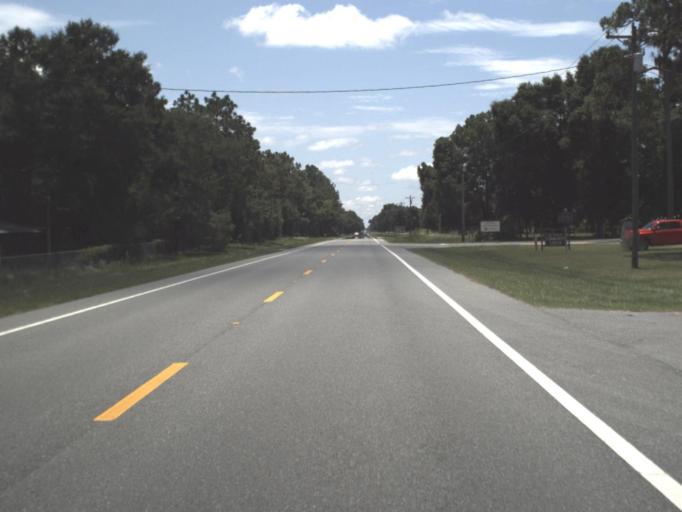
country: US
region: Florida
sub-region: Dixie County
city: Cross City
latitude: 29.7375
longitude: -82.9847
